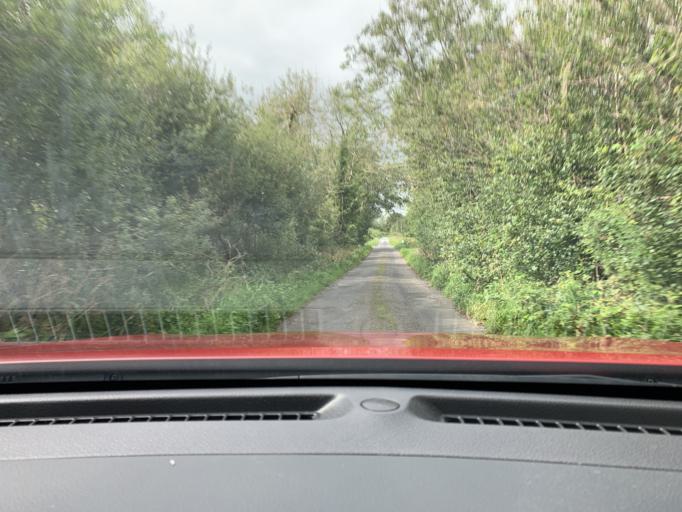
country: IE
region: Connaught
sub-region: Sligo
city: Collooney
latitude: 54.1572
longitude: -8.4280
